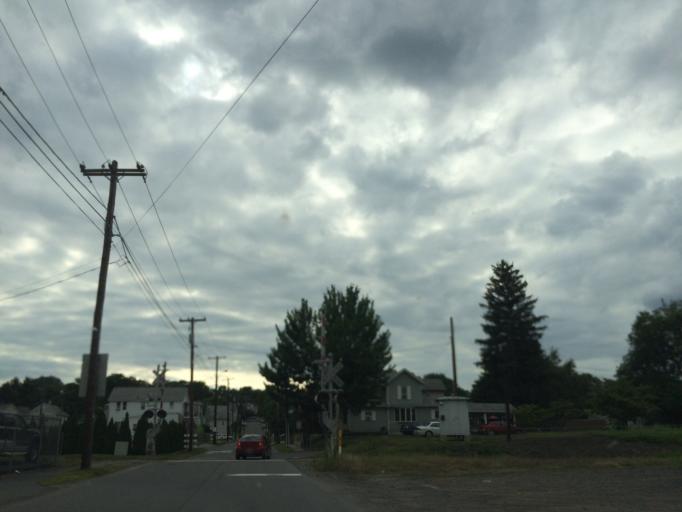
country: US
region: Pennsylvania
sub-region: Lackawanna County
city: Dunmore
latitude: 41.4413
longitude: -75.6431
